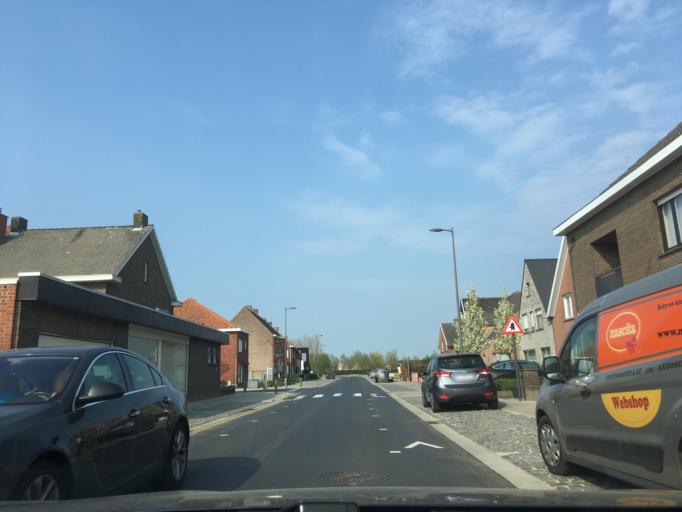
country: BE
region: Flanders
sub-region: Provincie West-Vlaanderen
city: Ardooie
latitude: 50.9840
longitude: 3.2023
